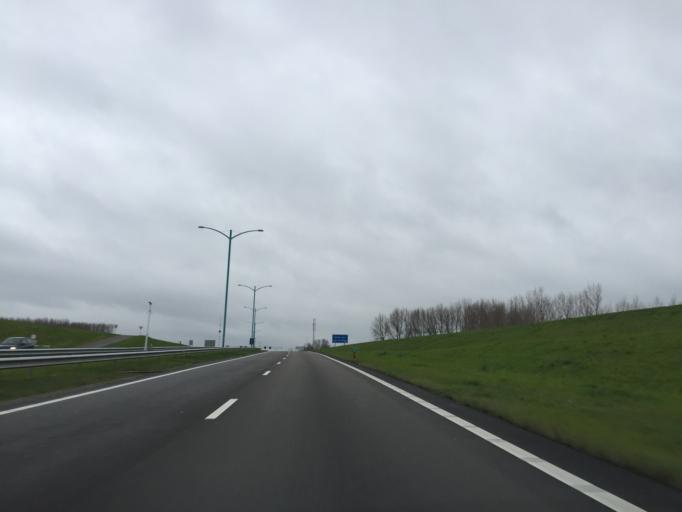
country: NL
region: Zeeland
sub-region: Gemeente Terneuzen
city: Terneuzen
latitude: 51.3372
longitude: 3.7989
